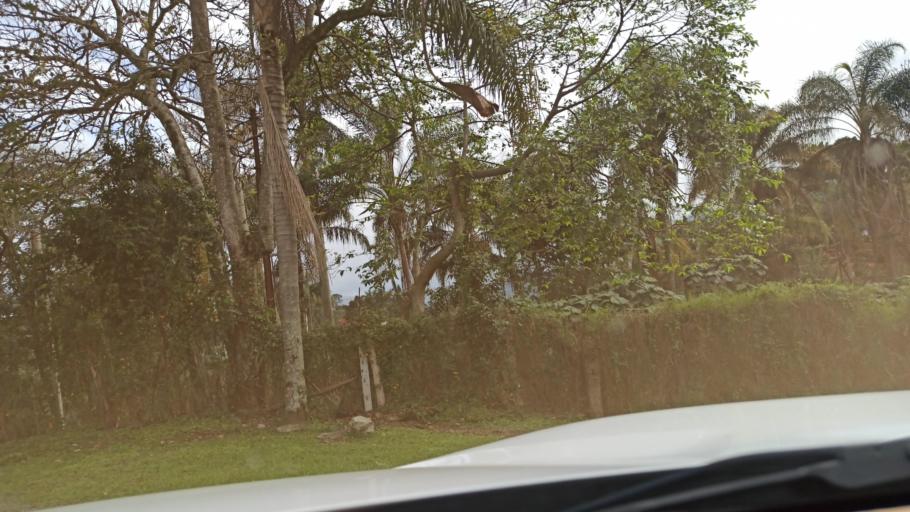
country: MX
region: Veracruz
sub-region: Fortin
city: Fortin de las Flores
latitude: 18.9024
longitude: -96.9933
